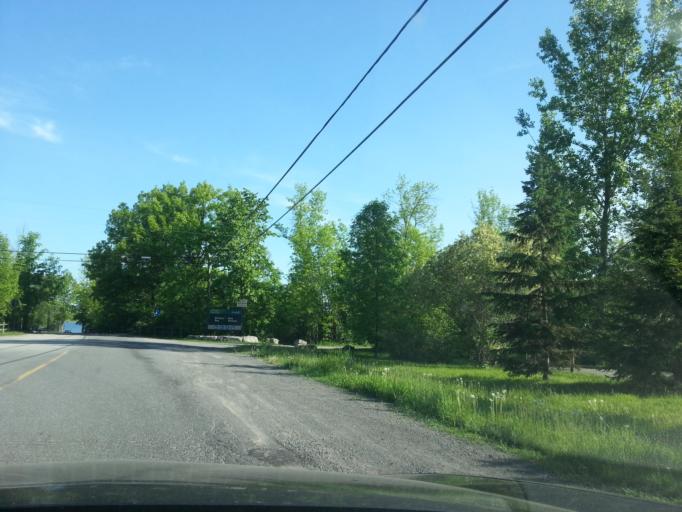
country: CA
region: Ontario
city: Bells Corners
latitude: 45.3644
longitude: -75.8829
